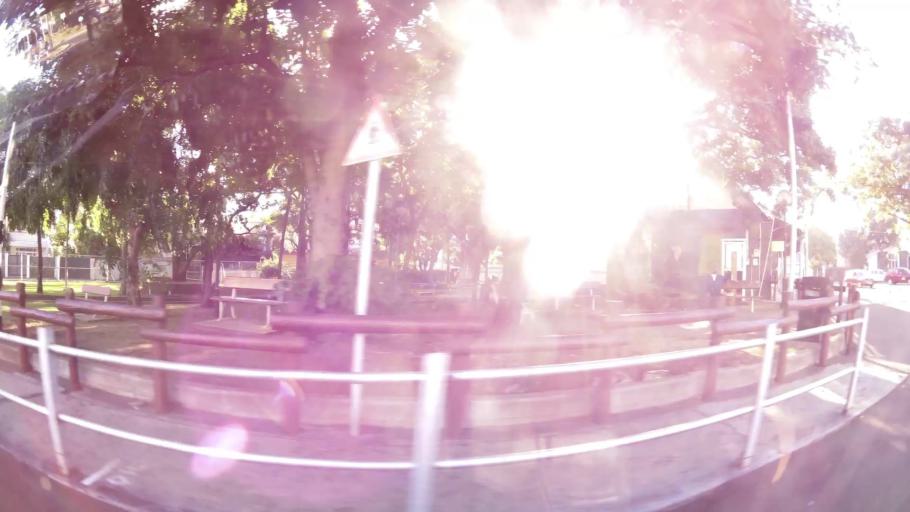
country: MU
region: Moka
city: Moka
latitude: -20.2269
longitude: 57.4678
